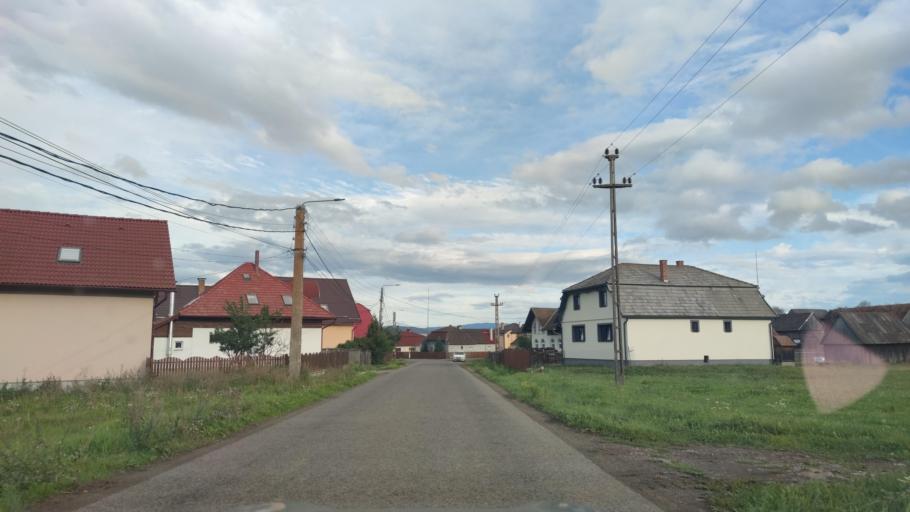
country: RO
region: Harghita
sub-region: Comuna Remetea
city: Remetea
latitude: 46.8011
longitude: 25.4408
